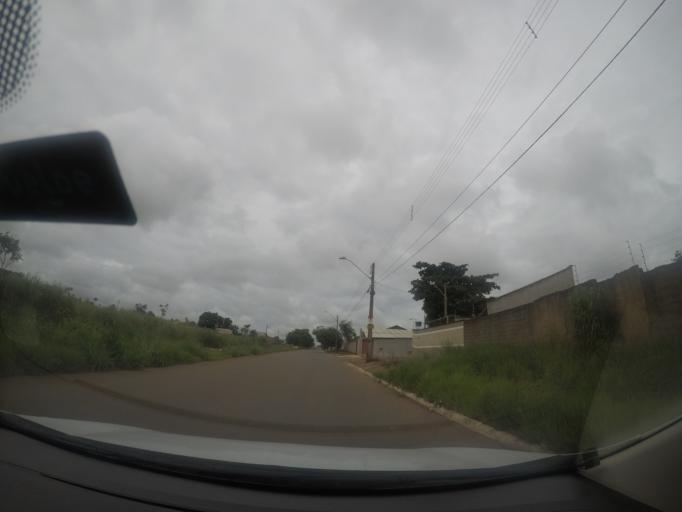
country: BR
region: Goias
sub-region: Trindade
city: Trindade
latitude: -16.6849
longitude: -49.4034
